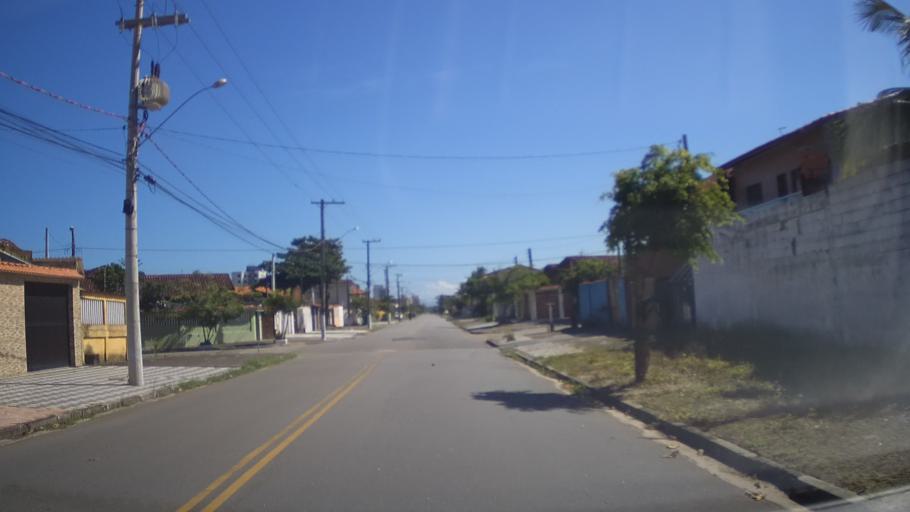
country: BR
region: Sao Paulo
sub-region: Mongagua
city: Mongagua
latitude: -24.1260
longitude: -46.6812
